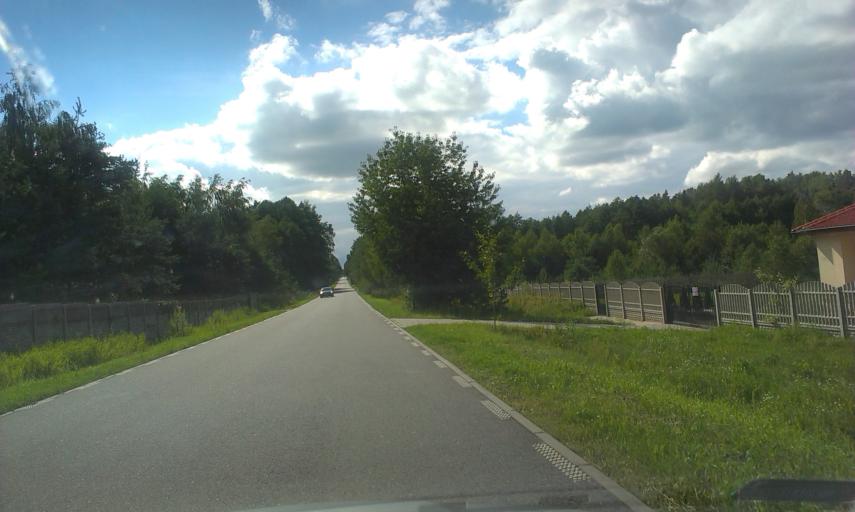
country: PL
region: Lodz Voivodeship
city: Zabia Wola
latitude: 51.9672
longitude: 20.6474
